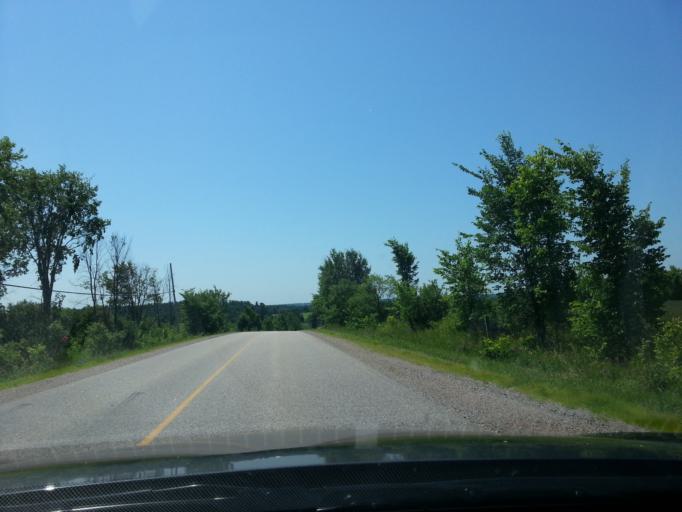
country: CA
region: Ontario
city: Arnprior
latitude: 45.5366
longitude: -76.3693
